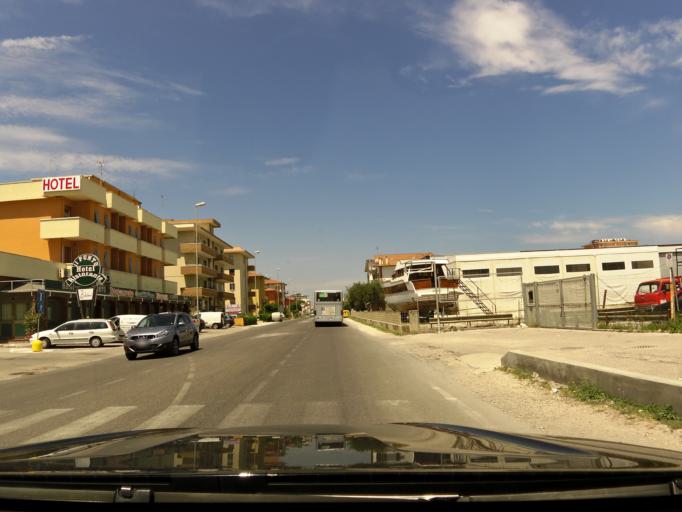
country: IT
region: The Marches
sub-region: Provincia di Pesaro e Urbino
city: Marotta
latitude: 43.7640
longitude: 13.1460
